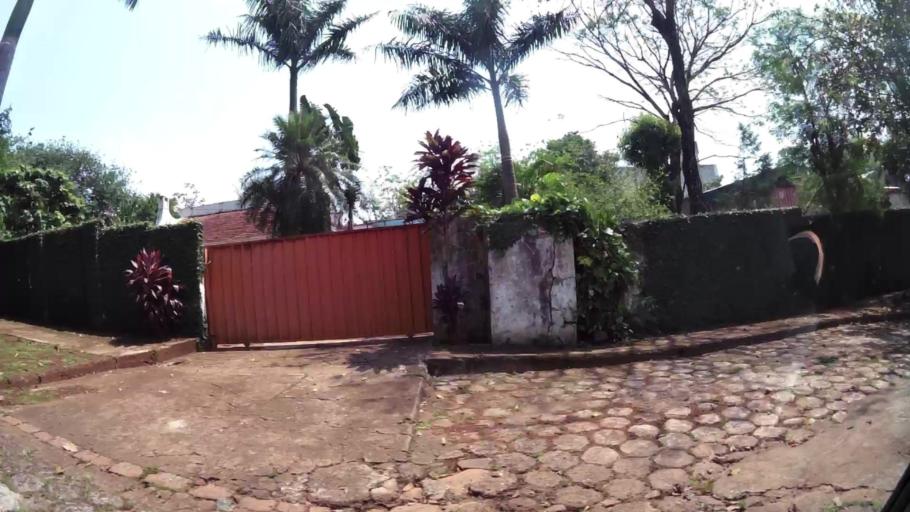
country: PY
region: Alto Parana
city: Presidente Franco
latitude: -25.5247
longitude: -54.6075
